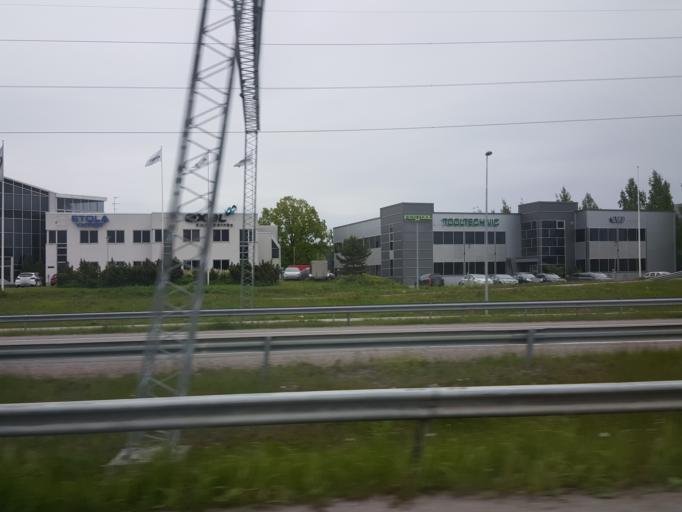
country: FI
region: Uusimaa
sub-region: Helsinki
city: Vantaa
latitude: 60.2916
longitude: 24.9820
